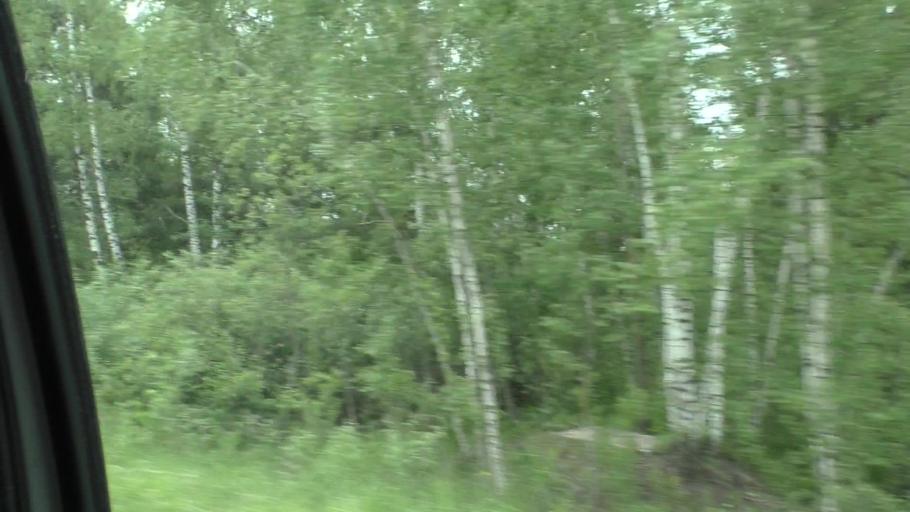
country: RU
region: Moskovskaya
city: Il'inskiy Pogost
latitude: 55.4686
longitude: 38.8979
